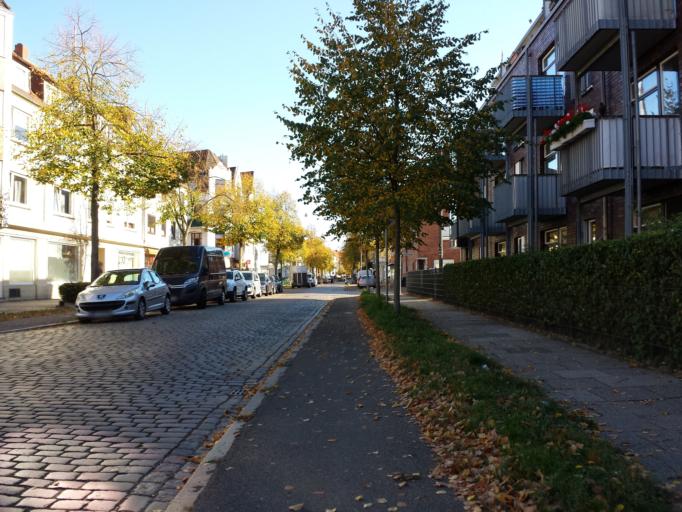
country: DE
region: Bremen
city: Bremen
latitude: 53.0970
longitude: 8.7828
